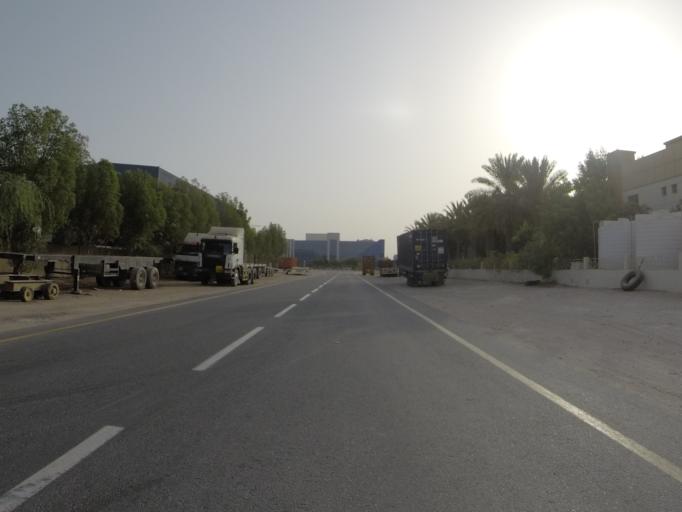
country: AE
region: Dubai
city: Dubai
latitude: 24.9522
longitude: 55.0644
